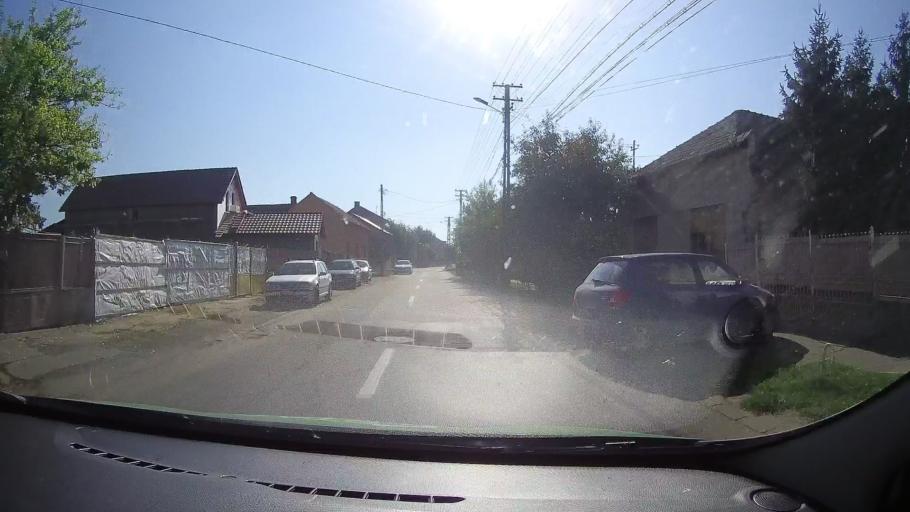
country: RO
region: Satu Mare
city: Carei
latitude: 47.6904
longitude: 22.4708
